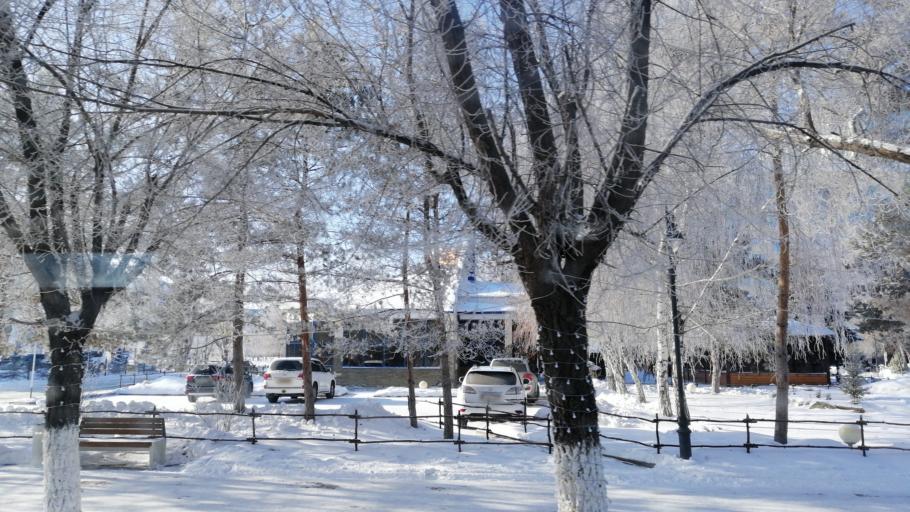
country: KZ
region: Aqtoebe
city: Aqtobe
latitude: 50.2978
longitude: 57.1563
